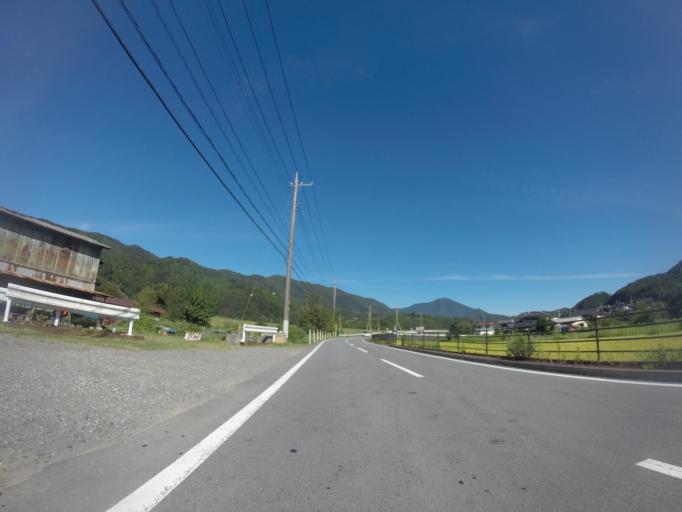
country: JP
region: Shizuoka
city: Fujinomiya
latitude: 35.3320
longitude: 138.4499
